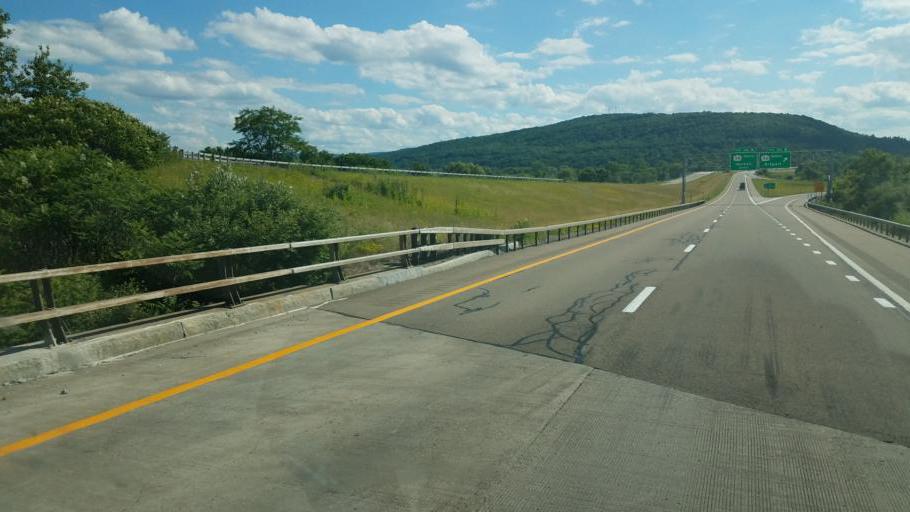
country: US
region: New York
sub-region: Steuben County
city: Hornell
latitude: 42.3756
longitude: -77.6713
